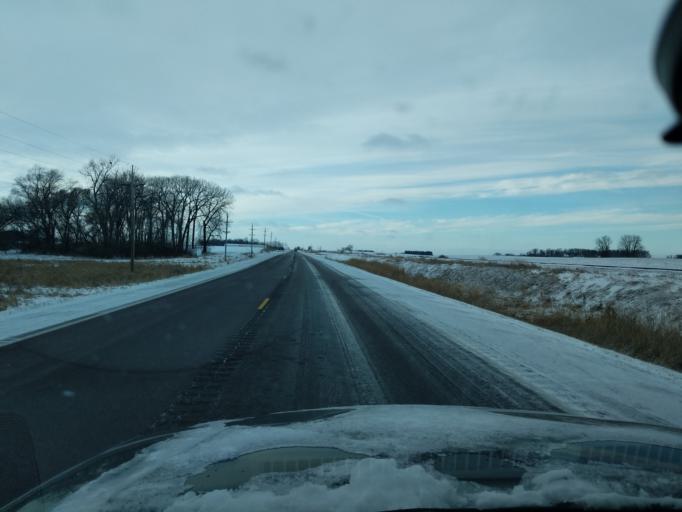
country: US
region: Minnesota
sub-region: Renville County
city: Hector
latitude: 44.7235
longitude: -94.5053
